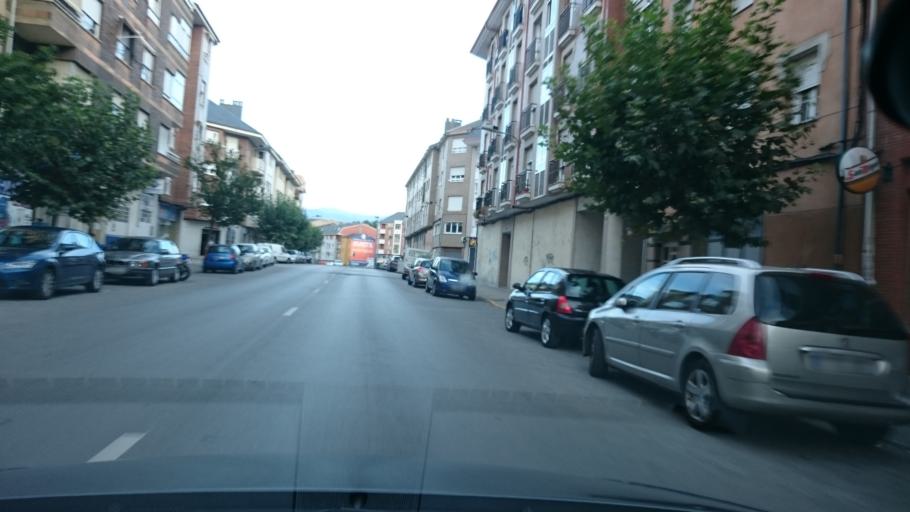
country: ES
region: Castille and Leon
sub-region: Provincia de Leon
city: Ponferrada
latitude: 42.5438
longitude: -6.6009
